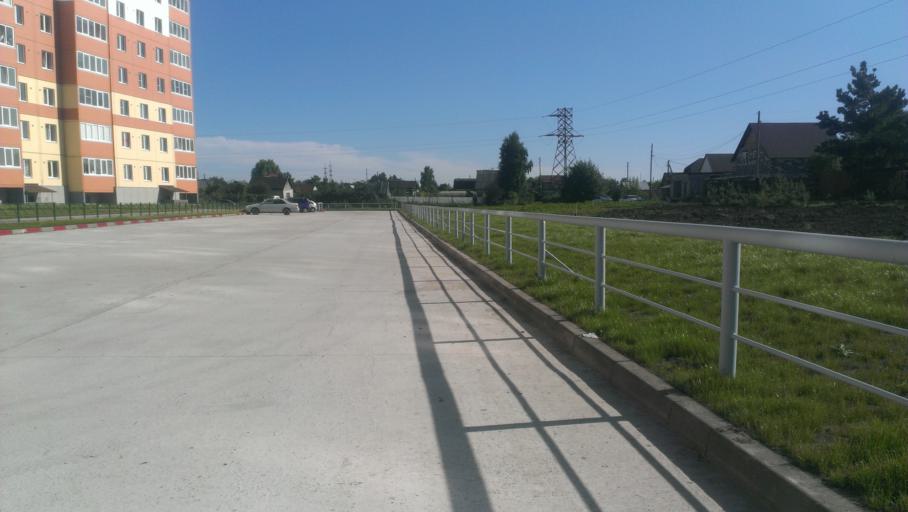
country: RU
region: Altai Krai
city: Novosilikatnyy
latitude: 53.3268
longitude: 83.6673
